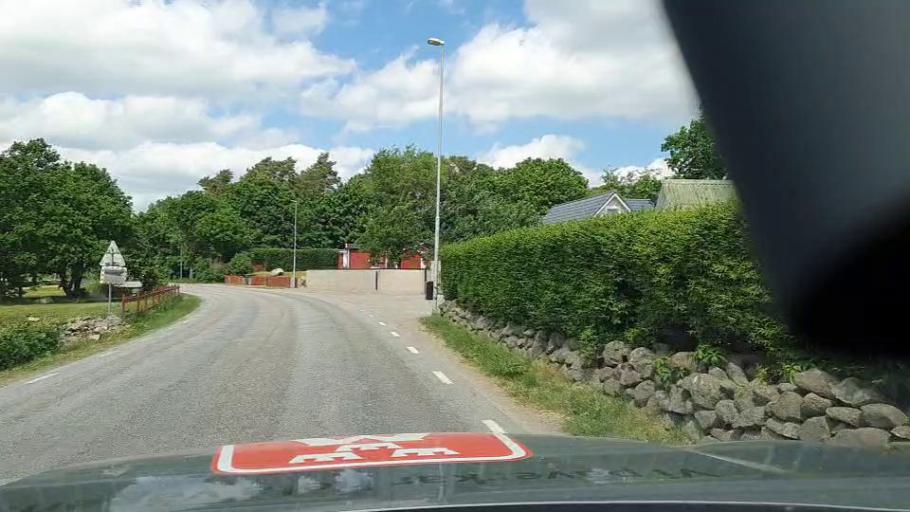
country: SE
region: Blekinge
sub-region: Karlshamns Kommun
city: Morrum
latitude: 56.1097
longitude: 14.6851
